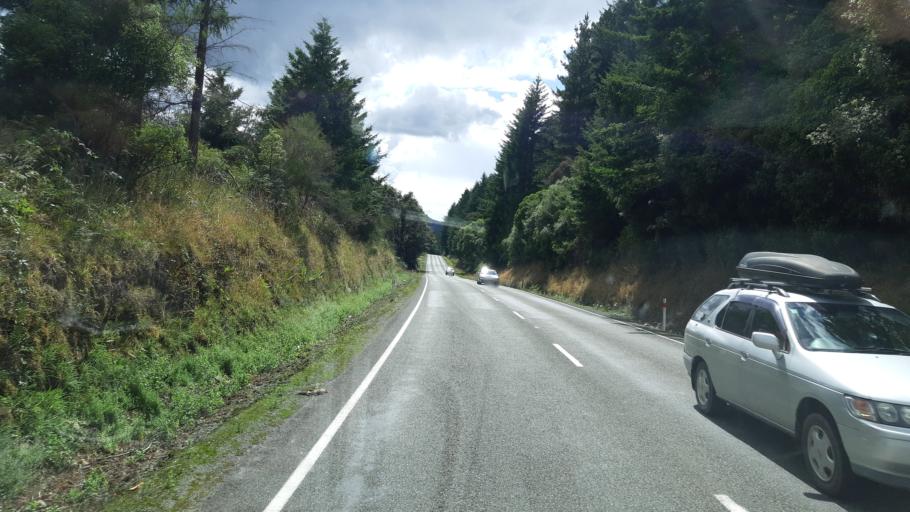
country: NZ
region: Tasman
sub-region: Tasman District
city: Wakefield
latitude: -41.5831
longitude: 172.7673
